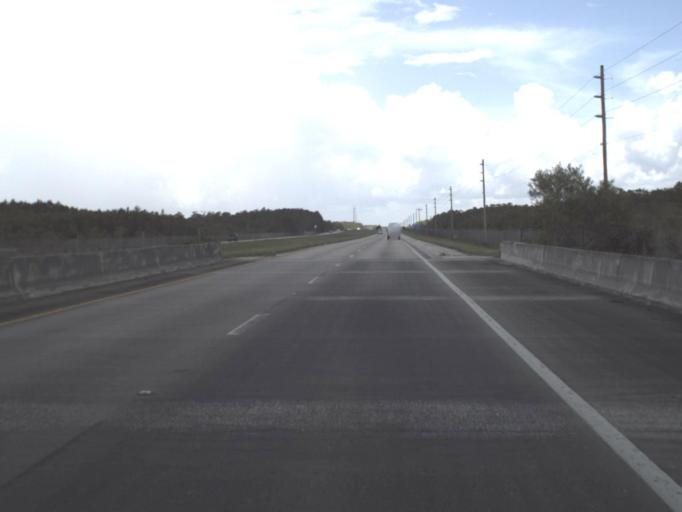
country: US
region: Florida
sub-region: Collier County
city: Immokalee
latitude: 26.1693
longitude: -81.0437
